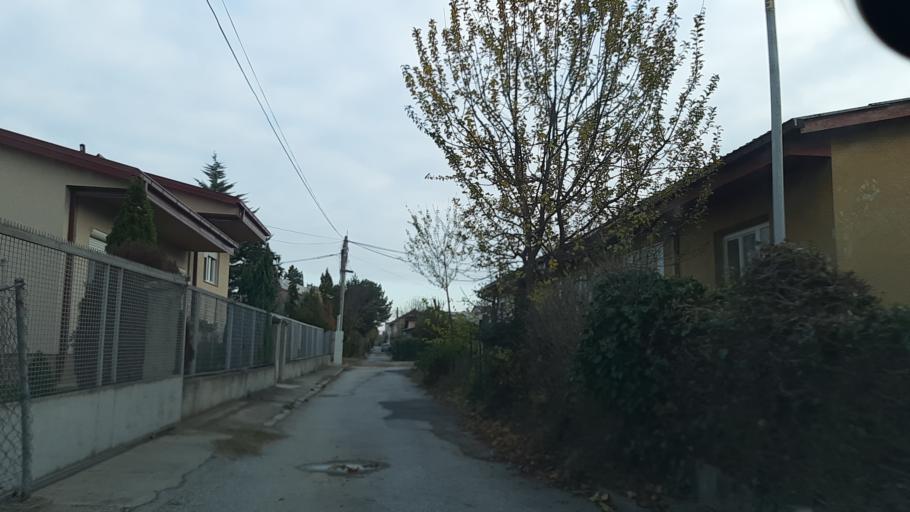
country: MK
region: Kisela Voda
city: Usje
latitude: 41.9750
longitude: 21.4559
